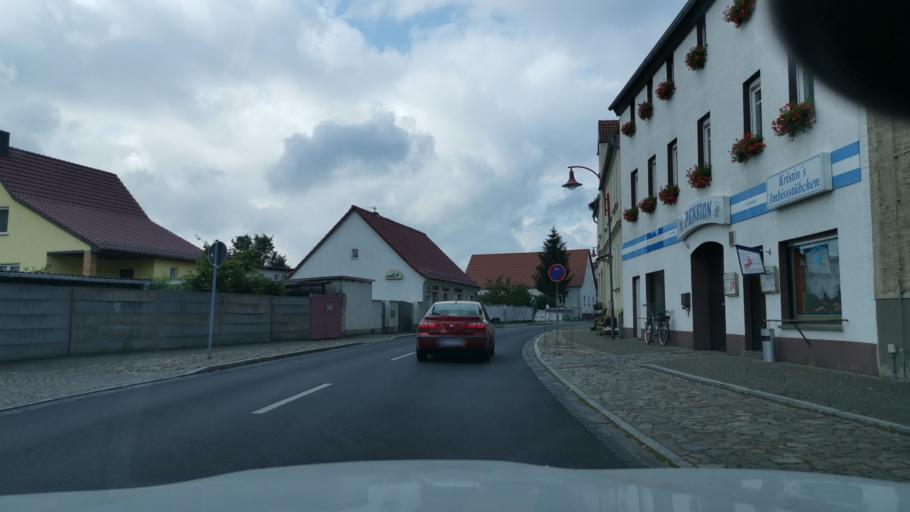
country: DE
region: Saxony-Anhalt
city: Annaburg
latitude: 51.7338
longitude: 13.0455
